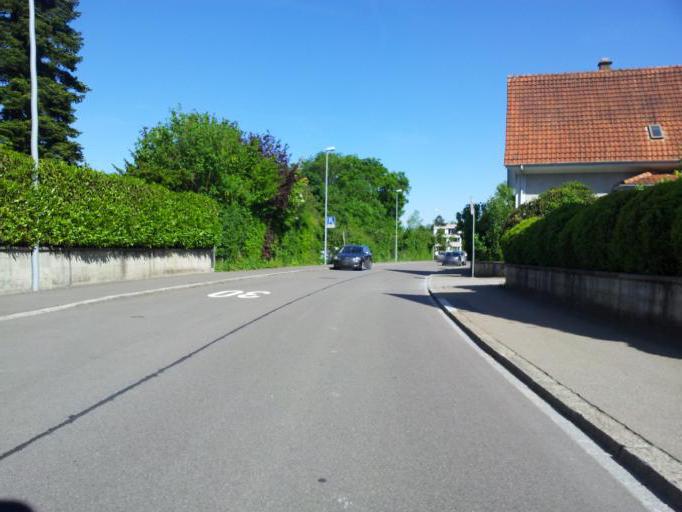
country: CH
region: Zurich
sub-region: Bezirk Dietikon
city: Dietikon / Kreuzacker
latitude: 47.3994
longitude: 8.4036
